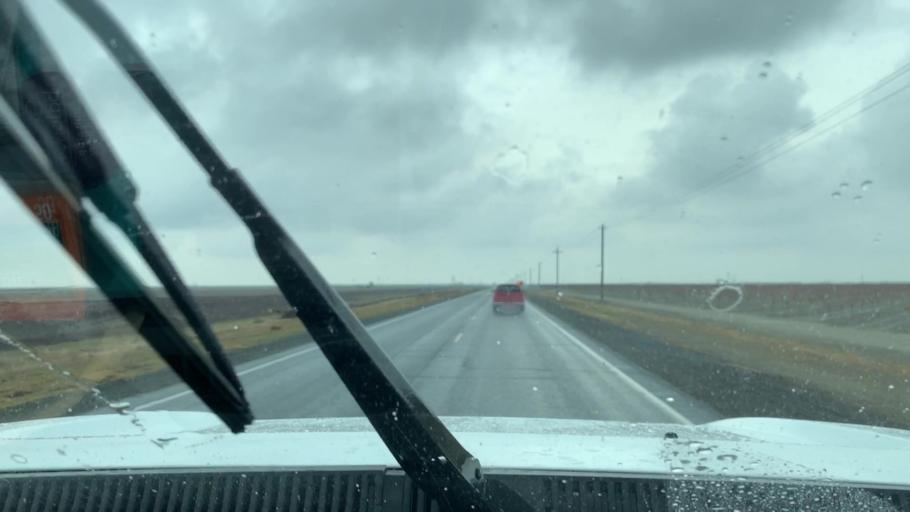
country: US
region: California
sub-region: Tulare County
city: Alpaugh
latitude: 36.0012
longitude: -119.4855
